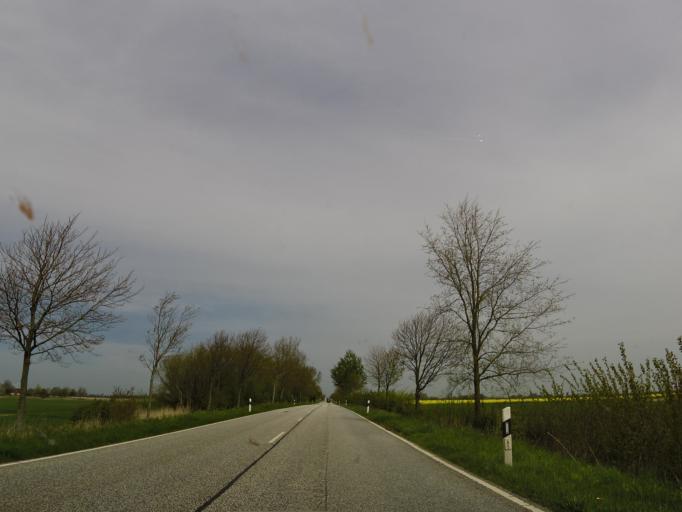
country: DE
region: Schleswig-Holstein
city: Oldenswort
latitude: 54.3610
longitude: 8.9748
